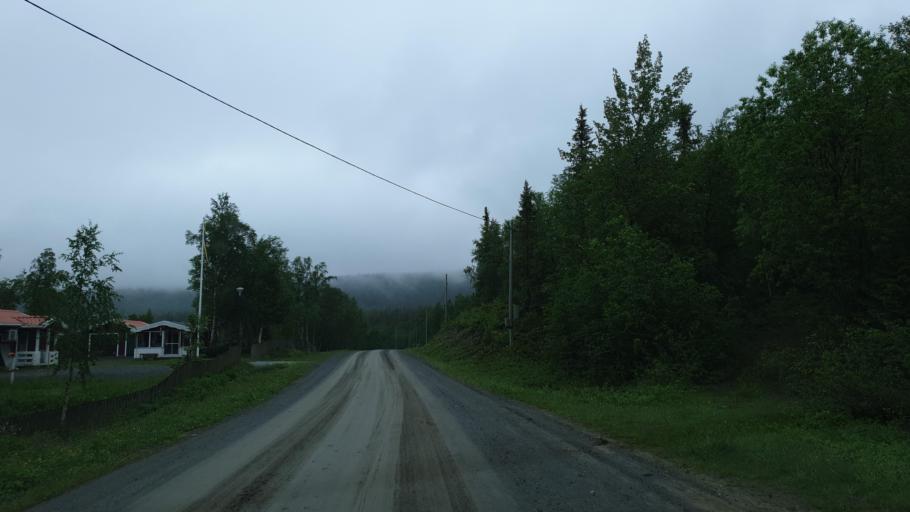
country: SE
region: Vaesterbotten
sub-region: Vilhelmina Kommun
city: Sjoberg
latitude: 65.3345
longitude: 15.8713
